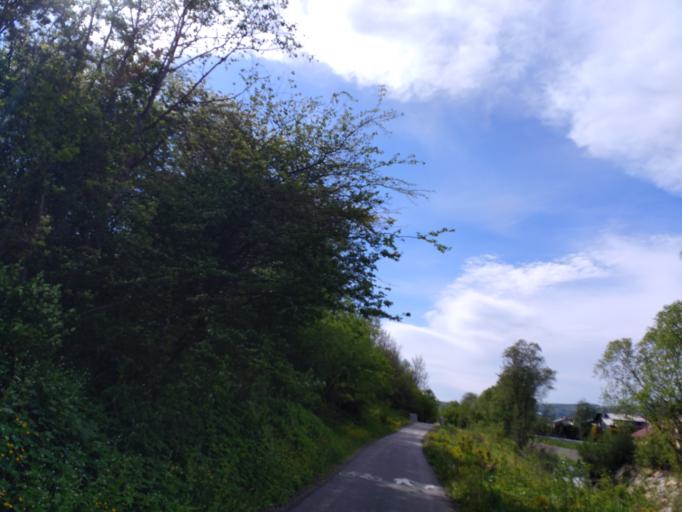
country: PL
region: Lesser Poland Voivodeship
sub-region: Powiat nowosadecki
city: Lacko
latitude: 49.5717
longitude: 20.4243
